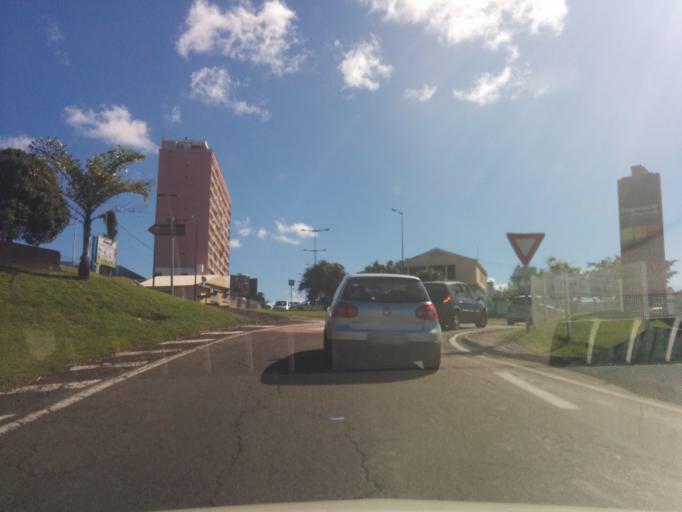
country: MQ
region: Martinique
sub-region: Martinique
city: Fort-de-France
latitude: 14.6050
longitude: -61.0883
